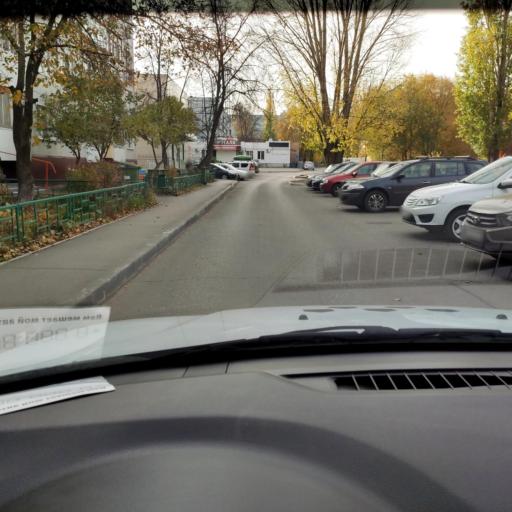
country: RU
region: Samara
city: Tol'yatti
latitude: 53.5090
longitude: 49.4367
